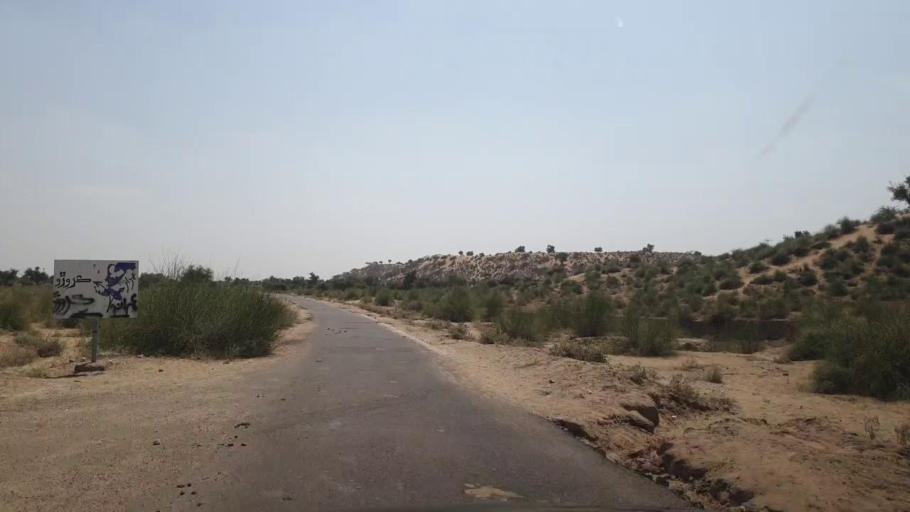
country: PK
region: Sindh
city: Islamkot
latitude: 25.1060
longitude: 70.7225
